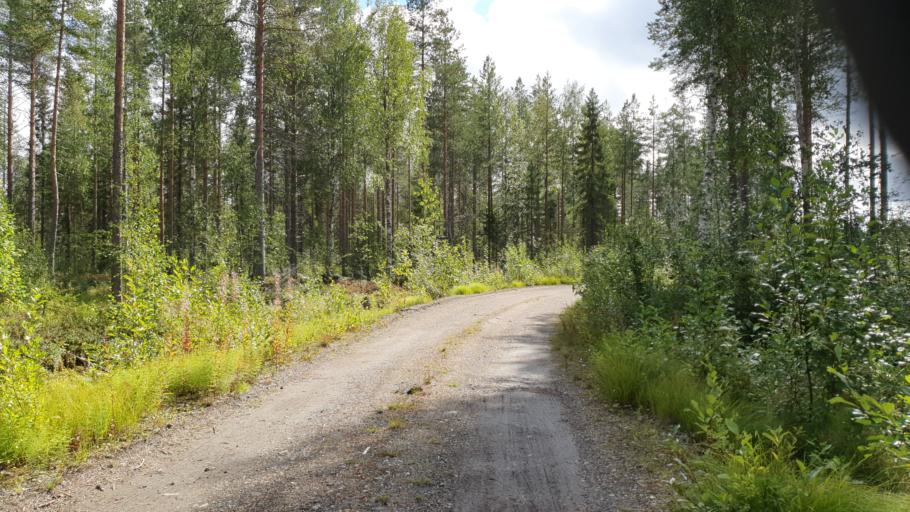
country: FI
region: Kainuu
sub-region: Kehys-Kainuu
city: Kuhmo
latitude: 64.1432
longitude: 29.3874
